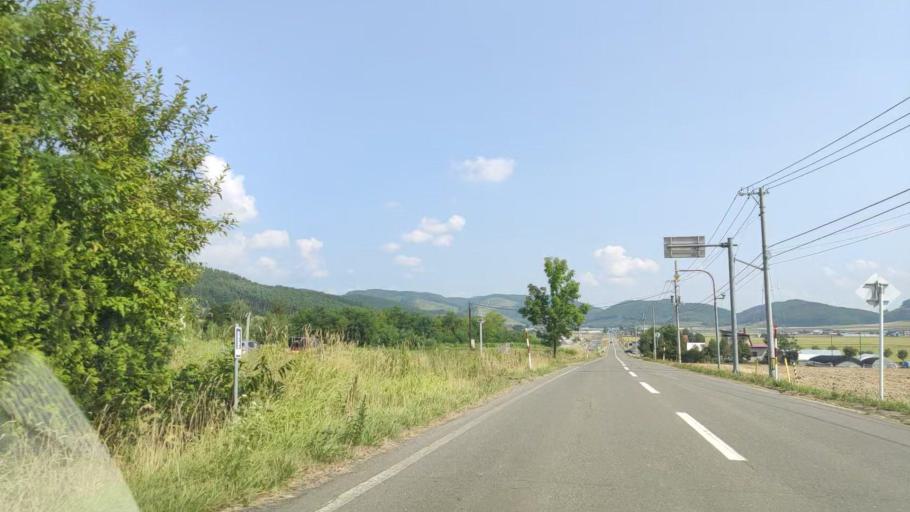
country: JP
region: Hokkaido
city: Shimo-furano
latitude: 43.3947
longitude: 142.3911
